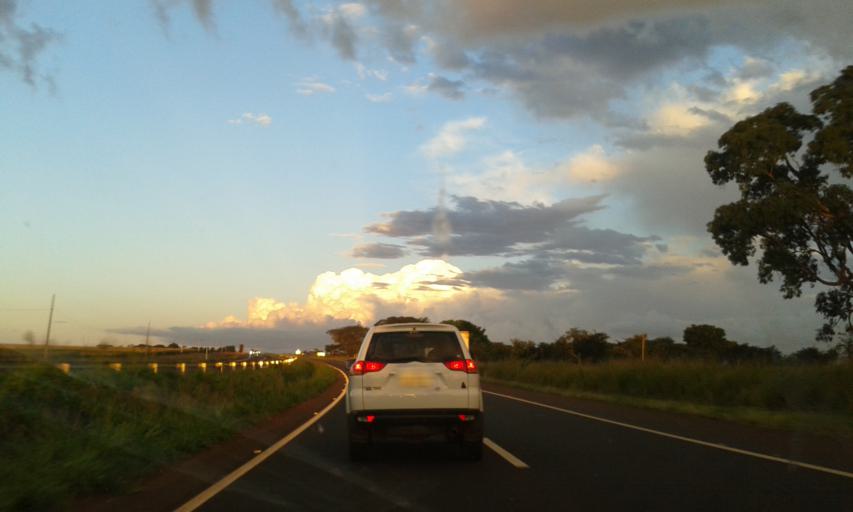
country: BR
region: Minas Gerais
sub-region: Monte Alegre De Minas
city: Monte Alegre de Minas
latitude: -18.8840
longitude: -48.7360
